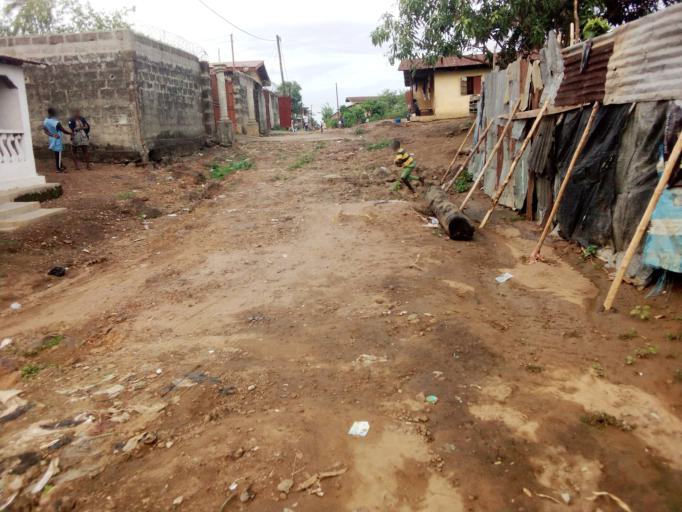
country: SL
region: Western Area
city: Waterloo
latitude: 8.3340
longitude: -13.0710
